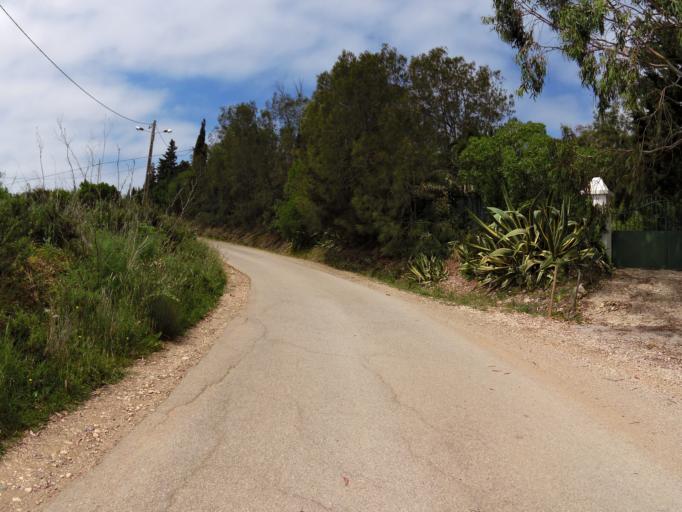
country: PT
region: Faro
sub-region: Vila do Bispo
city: Vila do Bispo
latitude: 37.0717
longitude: -8.8499
